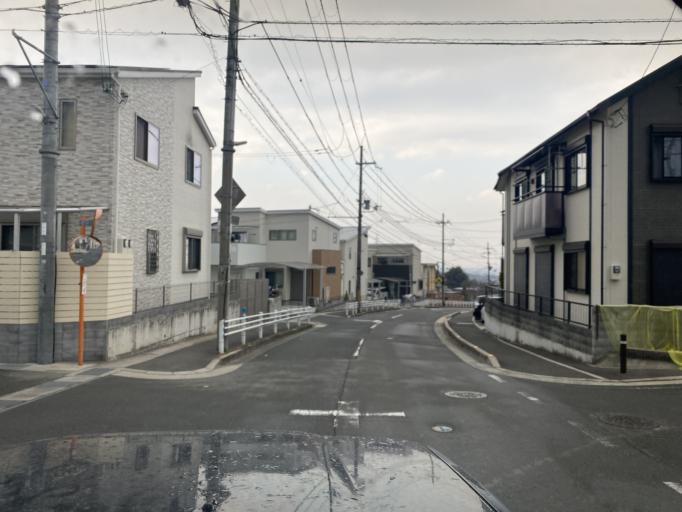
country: JP
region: Kyoto
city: Tanabe
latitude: 34.8185
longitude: 135.7549
